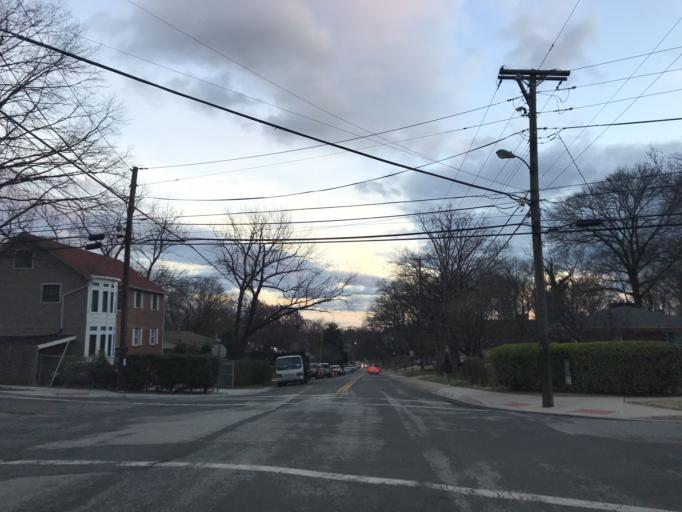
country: US
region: Maryland
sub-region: Prince George's County
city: Adelphi
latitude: 39.0123
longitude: -76.9798
